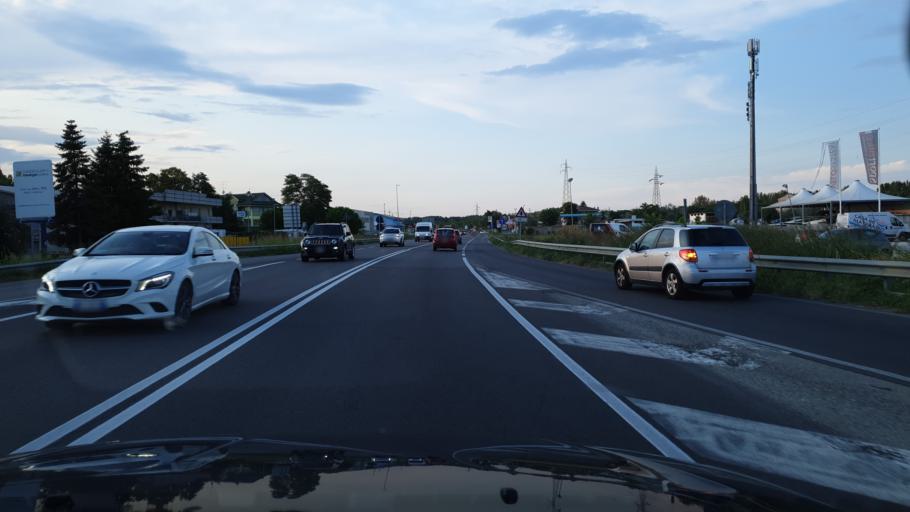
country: IT
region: Emilia-Romagna
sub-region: Forli-Cesena
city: Cesenatico
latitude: 44.1995
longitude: 12.3893
